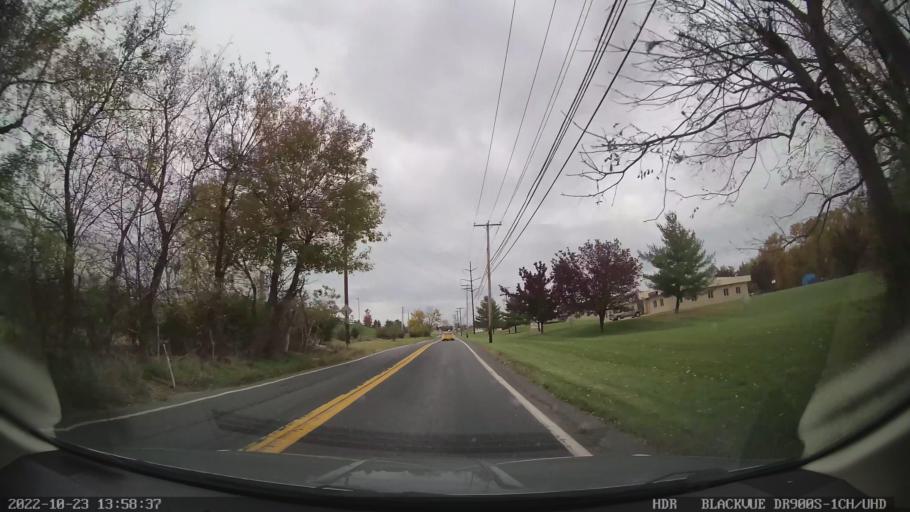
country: US
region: Pennsylvania
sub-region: Northampton County
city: Northampton
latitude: 40.6998
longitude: -75.4694
